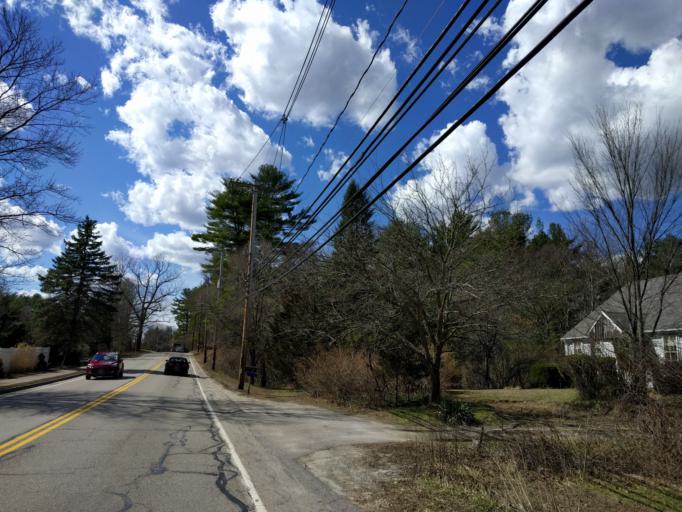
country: US
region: Massachusetts
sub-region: Norfolk County
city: Bellingham
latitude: 42.1123
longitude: -71.4805
